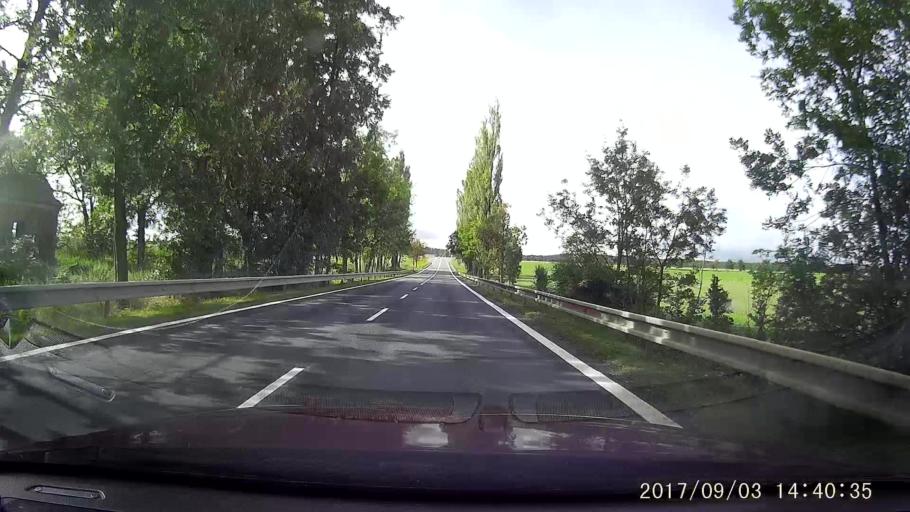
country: CZ
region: Vysocina
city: Zeletava
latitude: 49.0979
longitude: 15.7344
